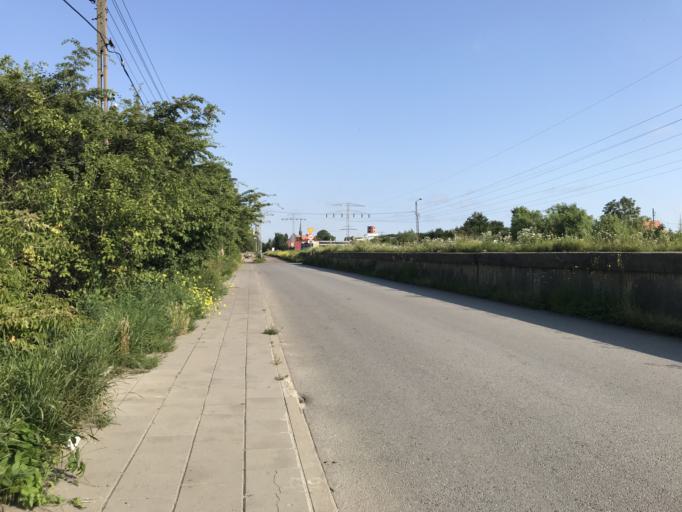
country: PL
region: Pomeranian Voivodeship
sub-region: Gdansk
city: Gdansk
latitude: 54.3452
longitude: 18.6804
